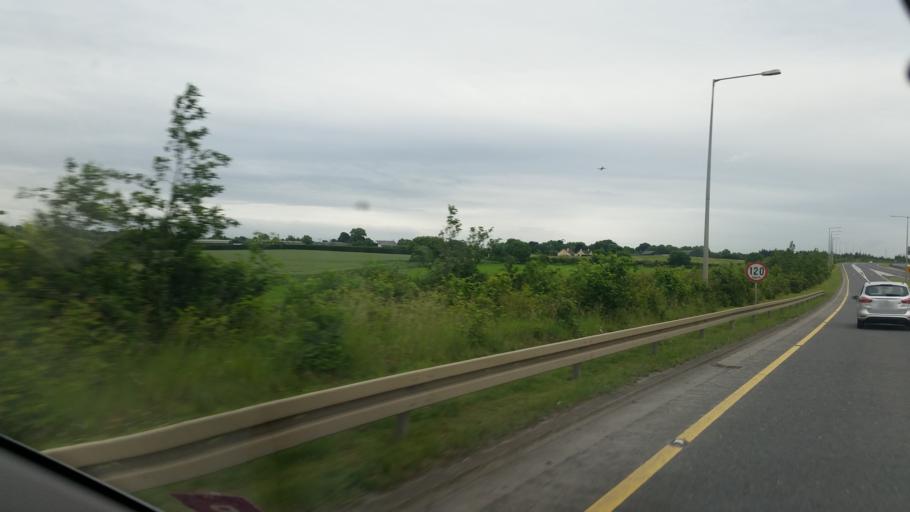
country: IE
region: Leinster
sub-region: Fingal County
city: Blanchardstown
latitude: 53.4313
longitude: -6.3416
